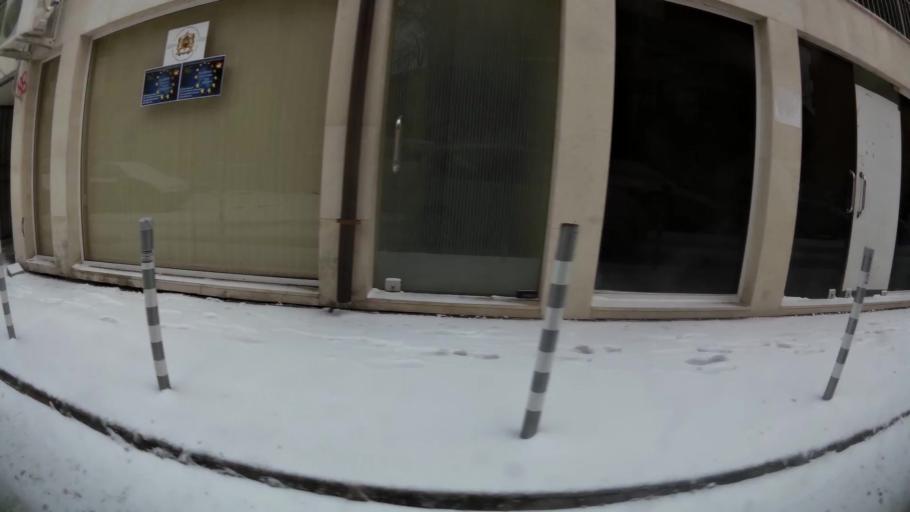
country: BG
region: Sofia-Capital
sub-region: Stolichna Obshtina
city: Sofia
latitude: 42.7037
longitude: 23.3121
